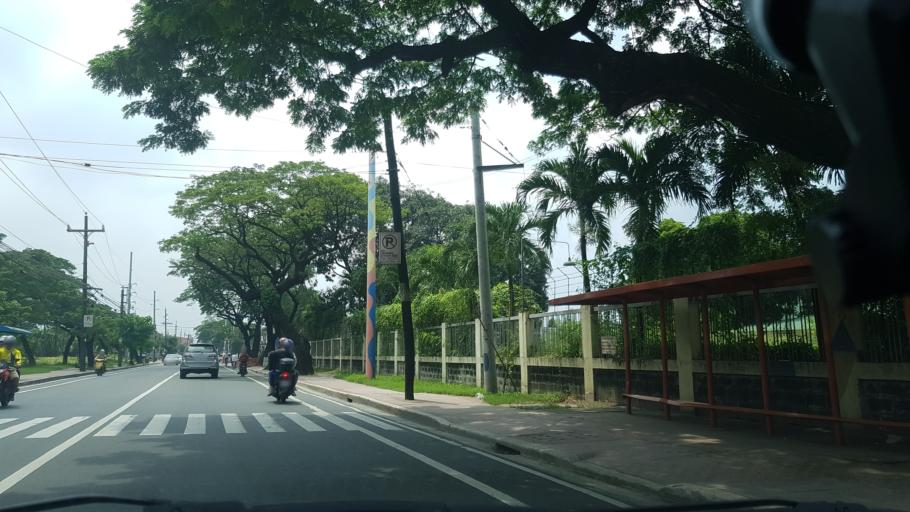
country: PH
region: Calabarzon
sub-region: Province of Rizal
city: San Mateo
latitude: 14.6675
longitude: 121.1076
